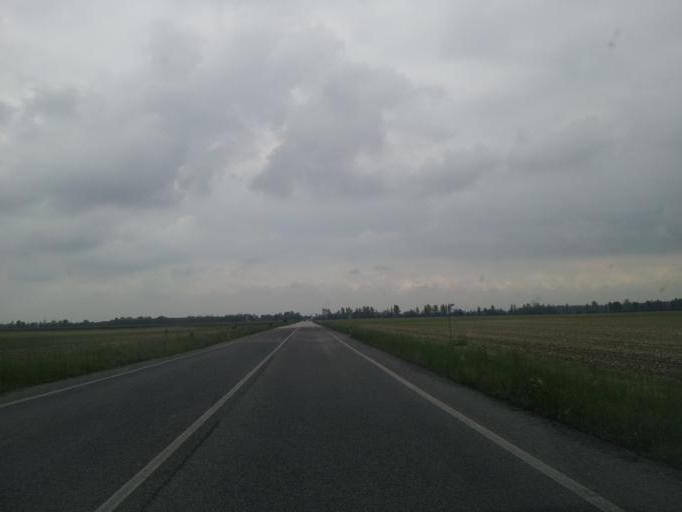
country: IT
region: Friuli Venezia Giulia
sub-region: Provincia di Udine
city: Varmo
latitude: 45.9226
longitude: 12.9895
